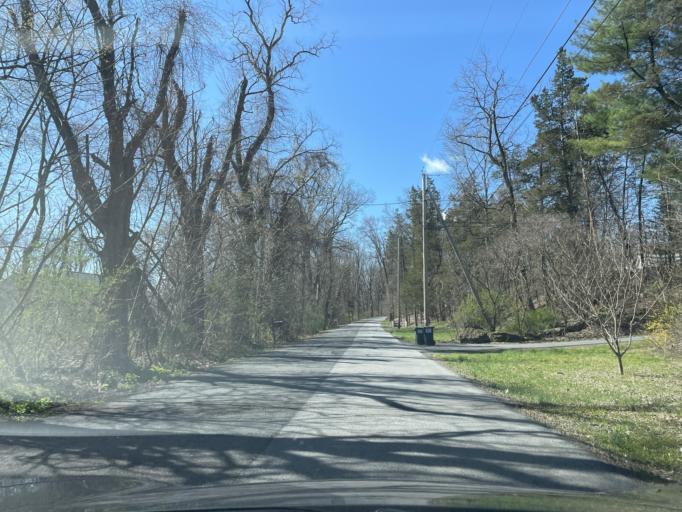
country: US
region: New York
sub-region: Ulster County
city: Saugerties South
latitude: 42.0553
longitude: -73.9903
